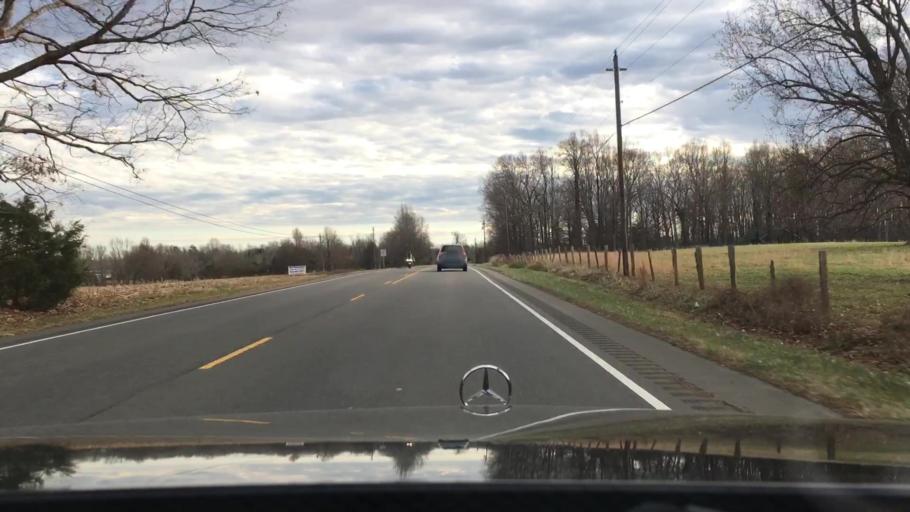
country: US
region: North Carolina
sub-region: Orange County
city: Hillsborough
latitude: 36.1647
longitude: -79.1304
